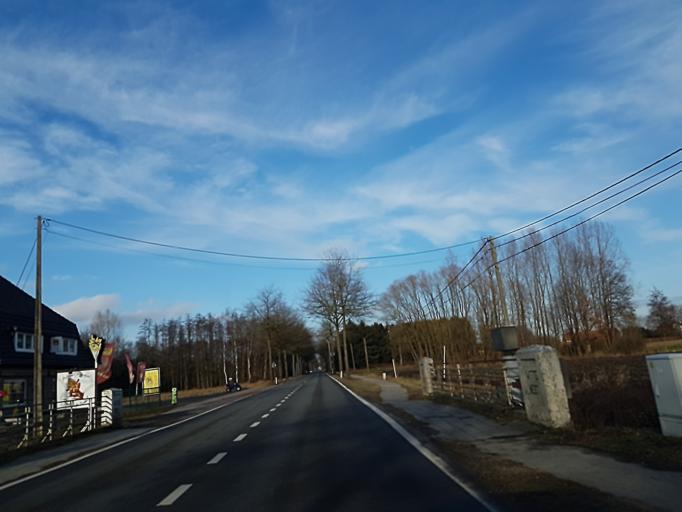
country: BE
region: Flanders
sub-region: Provincie Antwerpen
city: Retie
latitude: 51.2394
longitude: 5.0695
